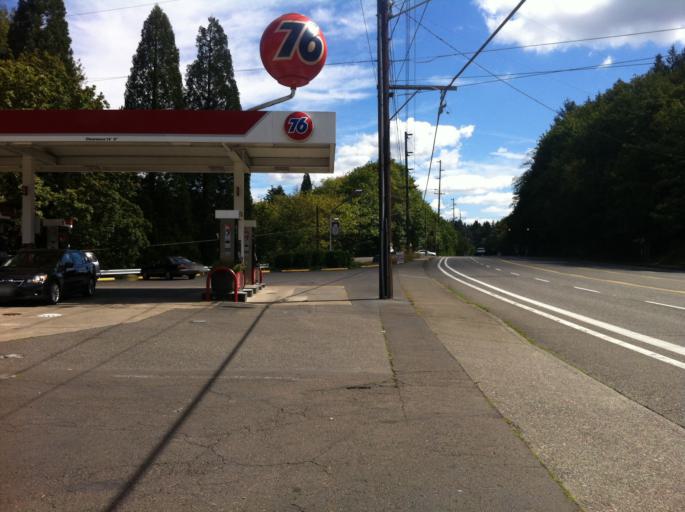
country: US
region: Oregon
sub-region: Washington County
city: Raleigh Hills
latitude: 45.4851
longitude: -122.7182
